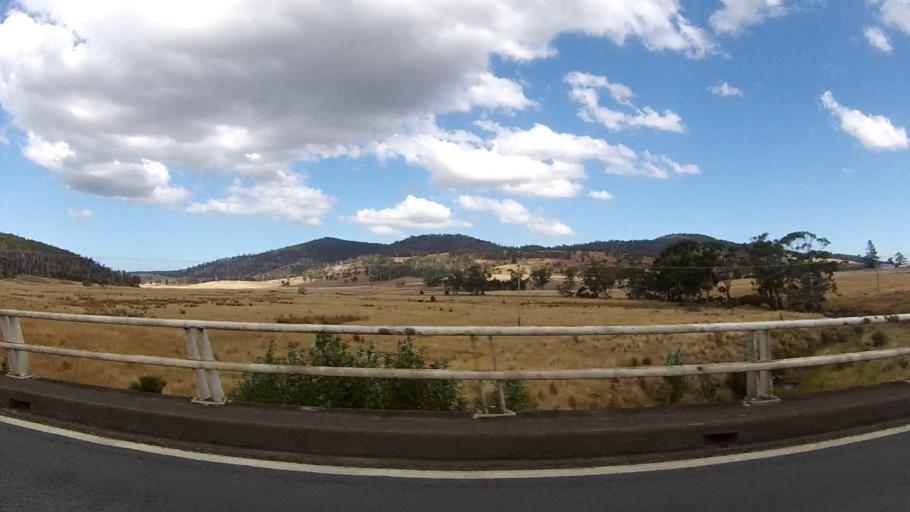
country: AU
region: Tasmania
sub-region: Sorell
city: Sorell
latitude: -42.6338
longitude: 147.6033
